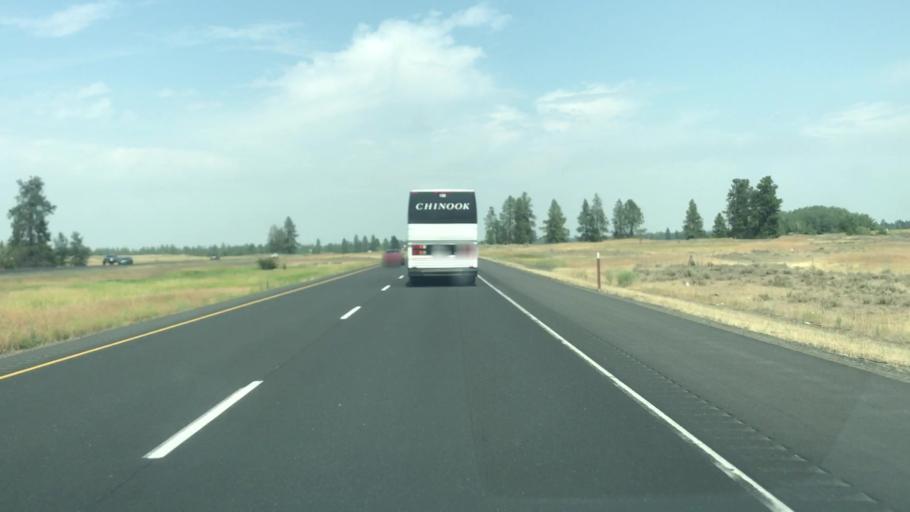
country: US
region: Washington
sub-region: Spokane County
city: Medical Lake
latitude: 47.4016
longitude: -117.8322
